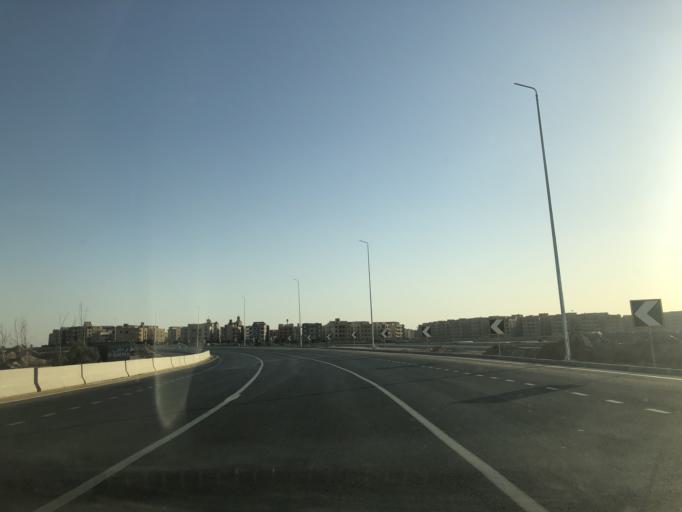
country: EG
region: Al Jizah
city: Madinat Sittah Uktubar
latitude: 29.9022
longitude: 31.0851
